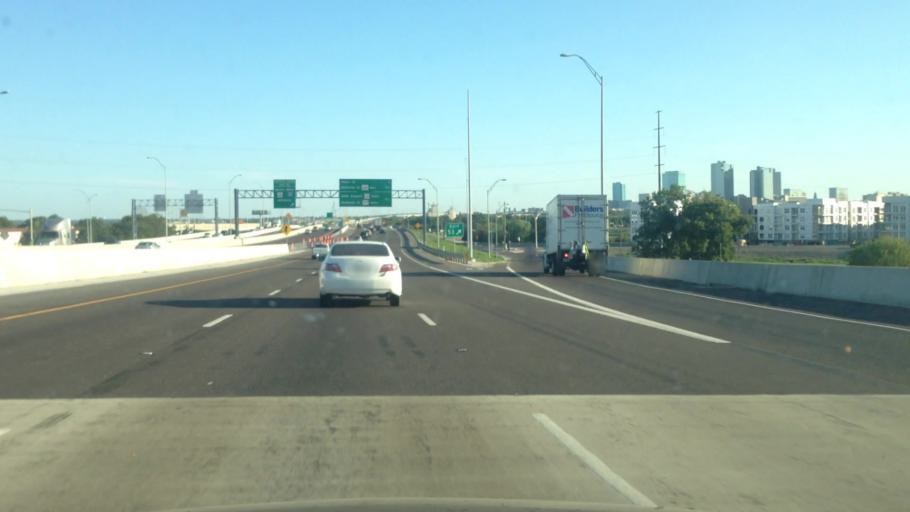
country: US
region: Texas
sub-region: Tarrant County
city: Haltom City
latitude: 32.7852
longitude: -97.3211
